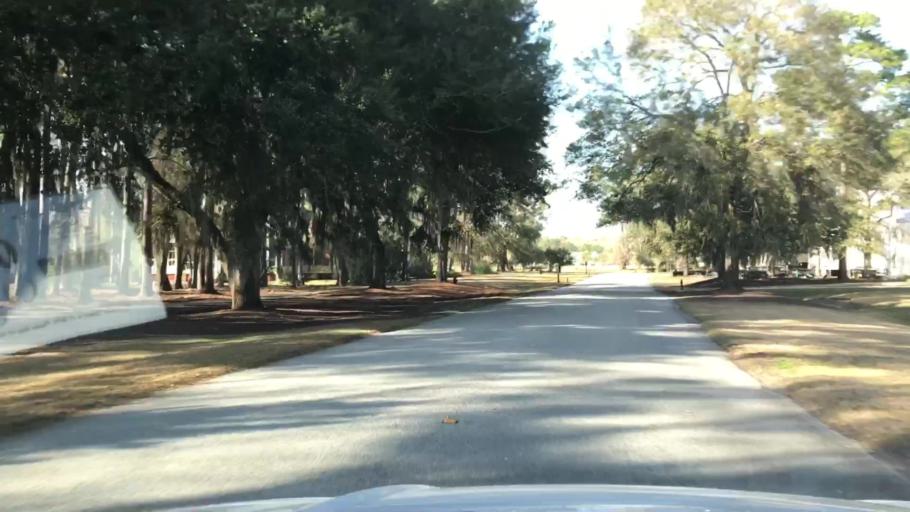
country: US
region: South Carolina
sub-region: Beaufort County
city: Bluffton
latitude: 32.3386
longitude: -80.9110
